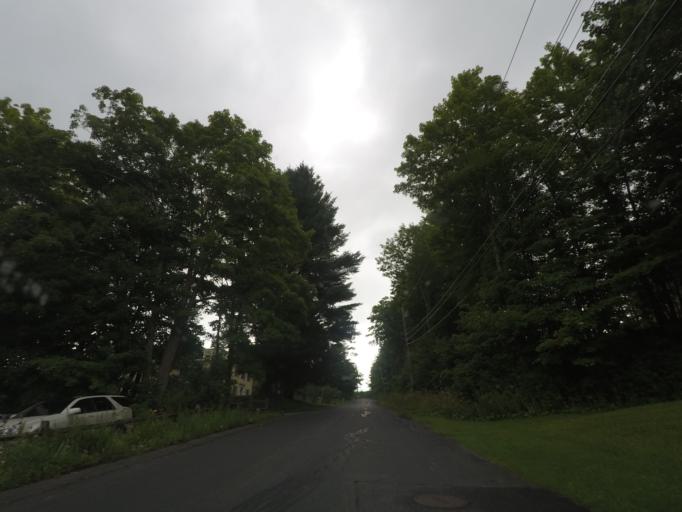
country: US
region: Massachusetts
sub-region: Berkshire County
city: Pittsfield
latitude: 42.4224
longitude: -73.3083
